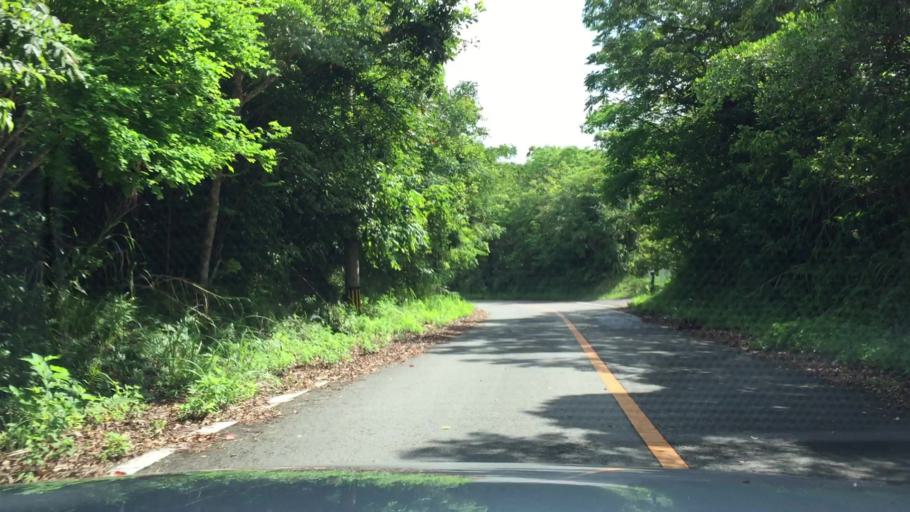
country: JP
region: Okinawa
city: Ishigaki
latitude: 24.3829
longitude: 124.1660
